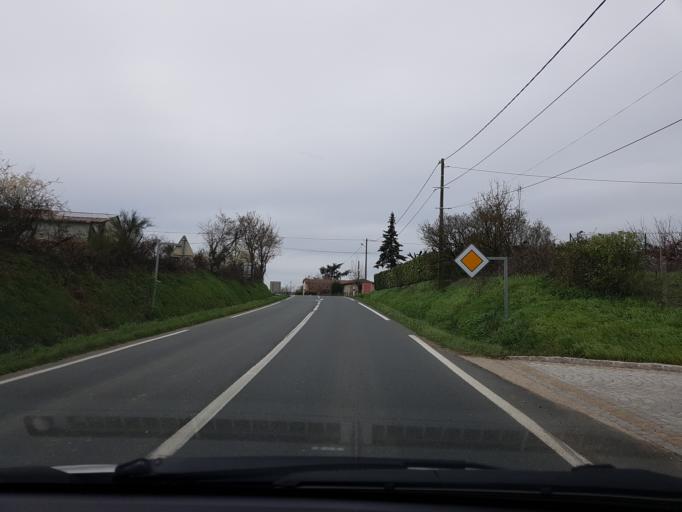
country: FR
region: Rhone-Alpes
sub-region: Departement de l'Ain
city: Trevoux
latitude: 45.9564
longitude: 4.7539
